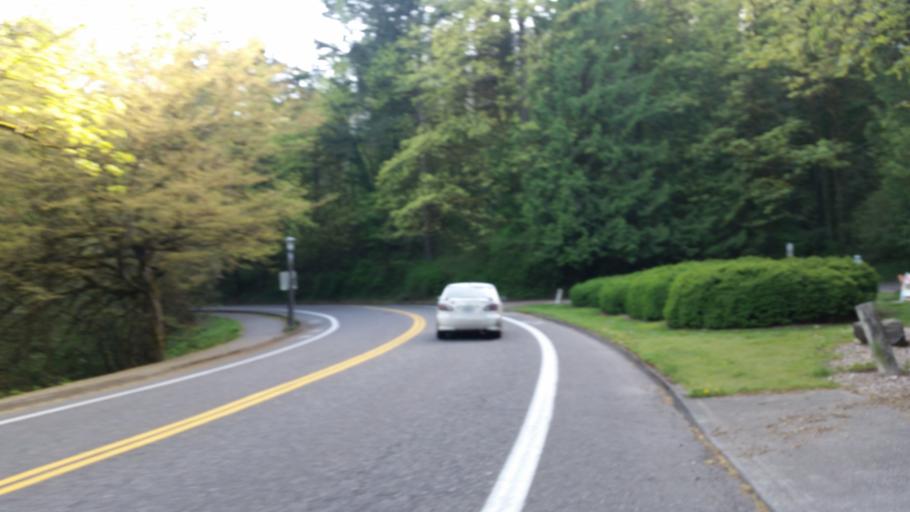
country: US
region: Oregon
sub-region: Multnomah County
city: Portland
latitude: 45.4847
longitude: -122.6844
